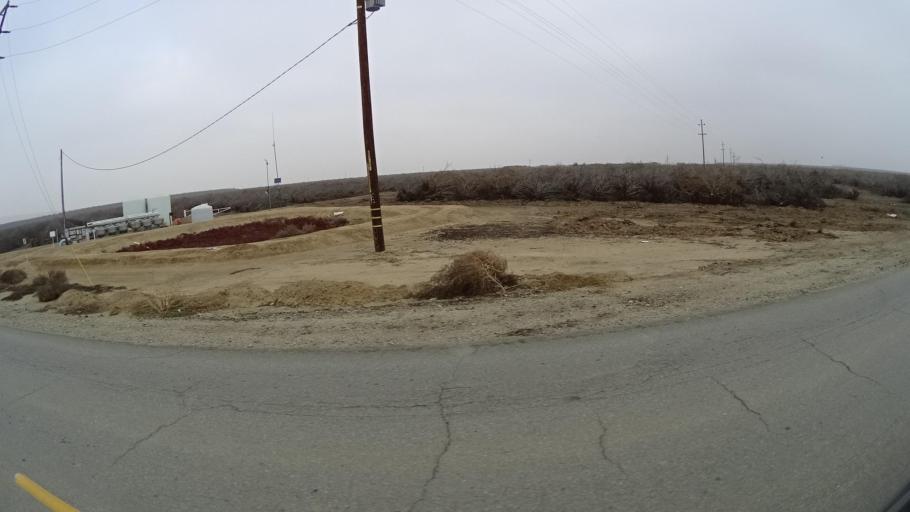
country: US
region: California
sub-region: Kern County
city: Maricopa
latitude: 35.1082
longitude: -119.3457
